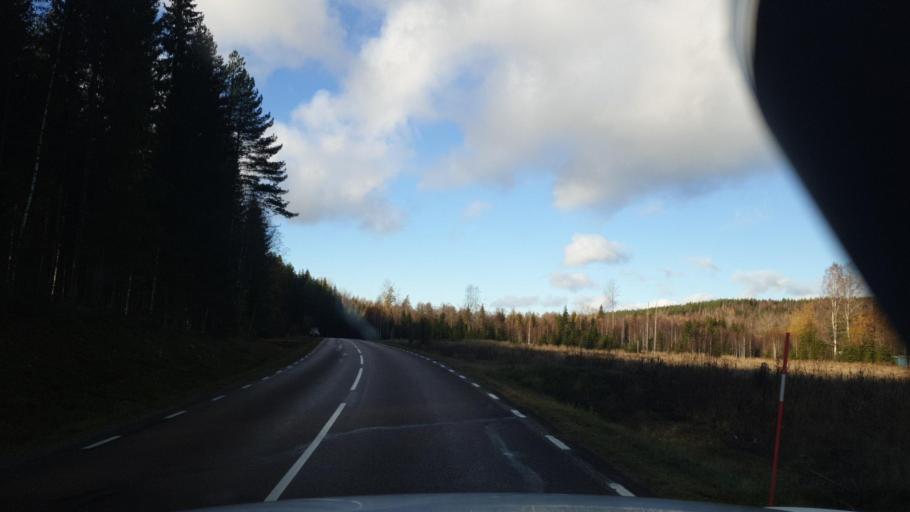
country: SE
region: Vaermland
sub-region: Arvika Kommun
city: Arvika
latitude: 59.4717
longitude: 12.8168
